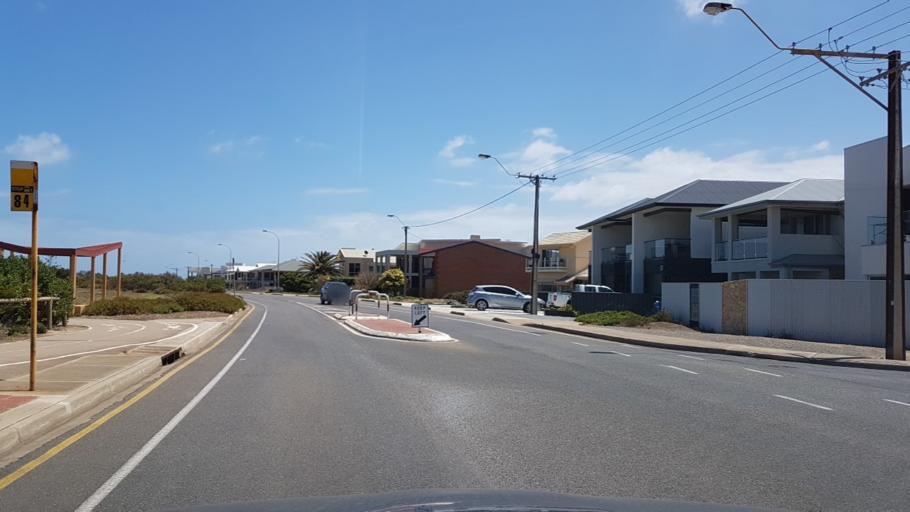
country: AU
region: South Australia
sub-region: Onkaparinga
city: Seaford
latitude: -35.1872
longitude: 138.4686
